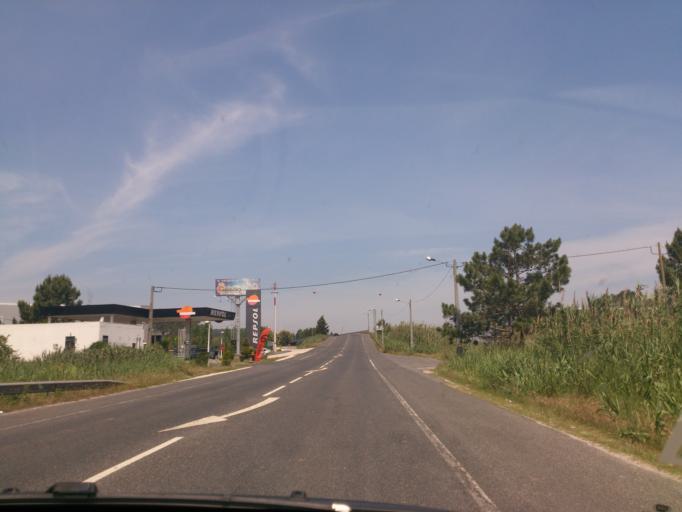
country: PT
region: Leiria
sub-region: Alcobaca
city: Alcobaca
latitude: 39.5828
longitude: -9.0119
